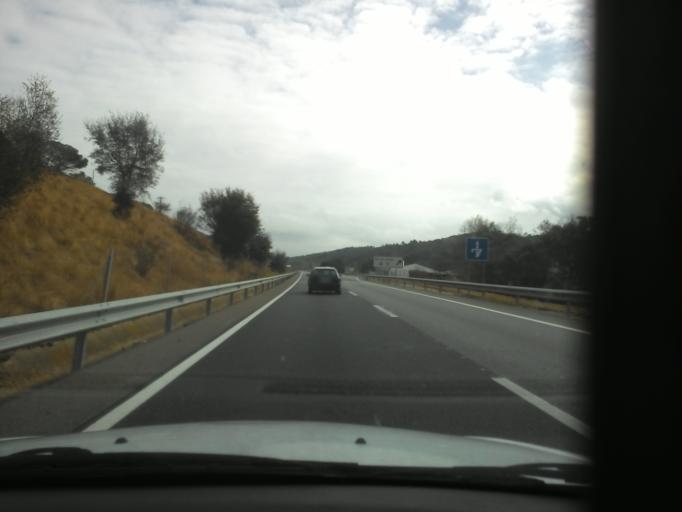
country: ES
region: Catalonia
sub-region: Provincia de Girona
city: Llagostera
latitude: 41.8279
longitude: 2.9414
